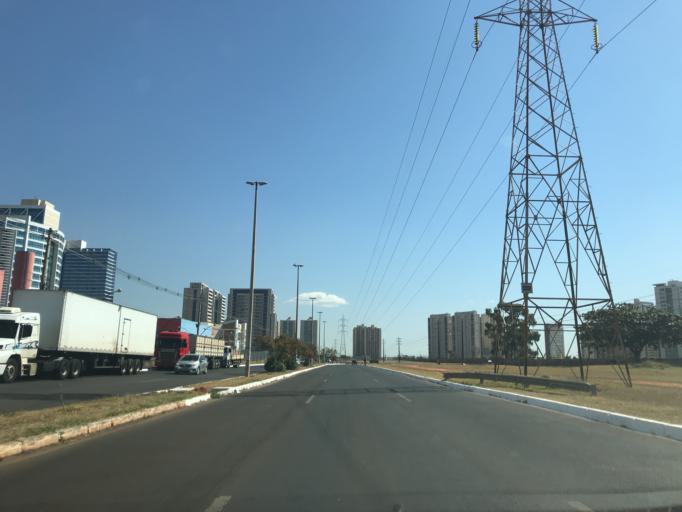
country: BR
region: Federal District
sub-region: Brasilia
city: Brasilia
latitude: -15.8433
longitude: -48.0412
